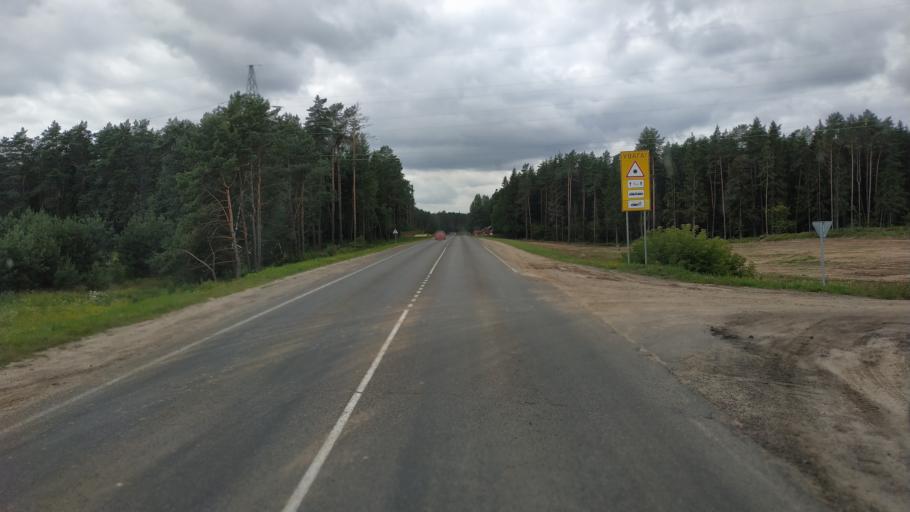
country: BY
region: Mogilev
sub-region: Mahilyowski Rayon
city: Veyno
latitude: 53.8761
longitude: 30.4268
